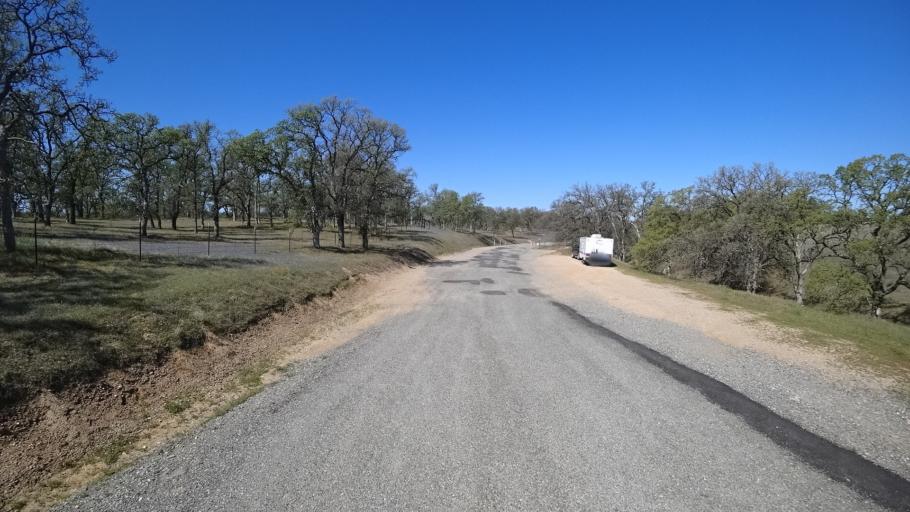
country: US
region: California
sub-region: Glenn County
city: Orland
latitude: 39.7686
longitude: -122.3517
